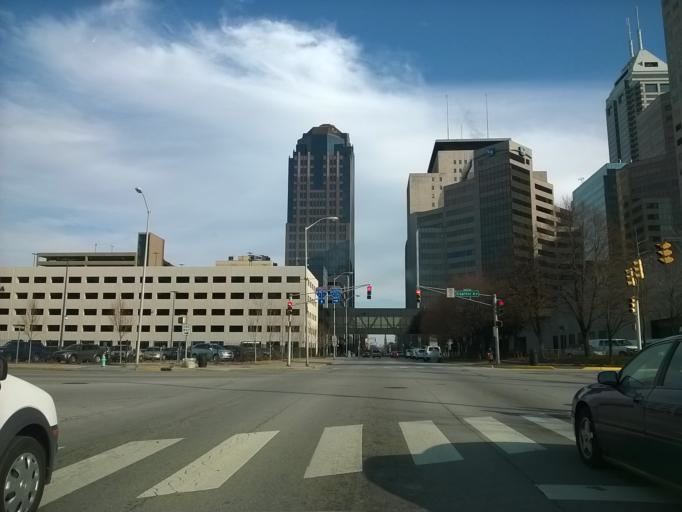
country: US
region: Indiana
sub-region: Marion County
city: Indianapolis
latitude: 39.7714
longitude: -86.1619
